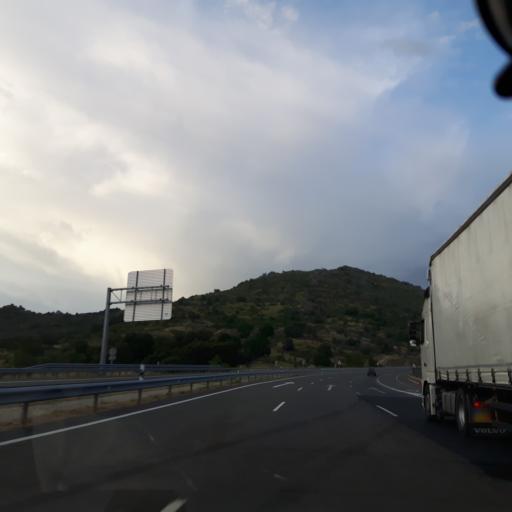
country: ES
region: Castille and Leon
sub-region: Provincia de Salamanca
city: Fresnedoso
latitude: 40.4336
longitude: -5.6947
